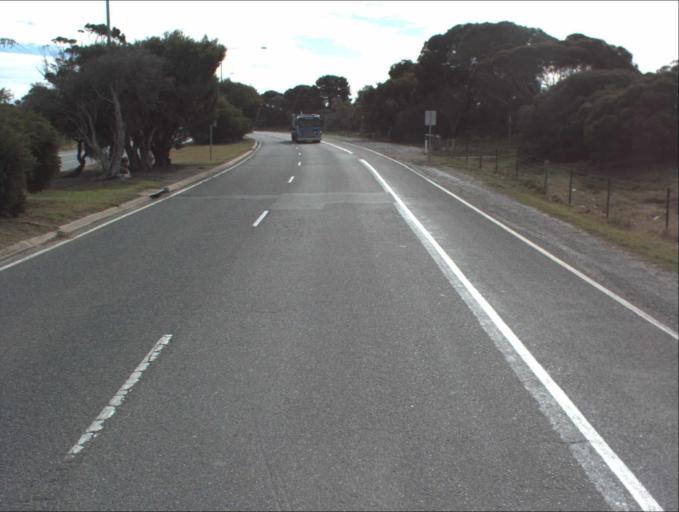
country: AU
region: South Australia
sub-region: Port Adelaide Enfield
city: Birkenhead
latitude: -34.7862
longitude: 138.5016
